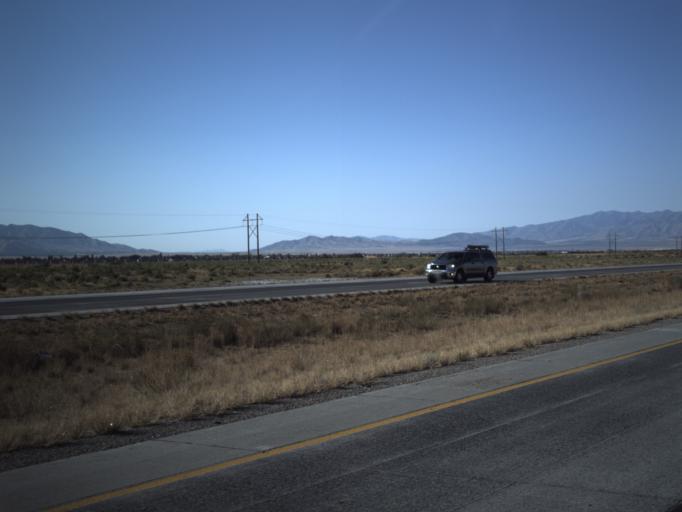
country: US
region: Utah
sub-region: Tooele County
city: Stansbury park
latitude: 40.6716
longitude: -112.2948
